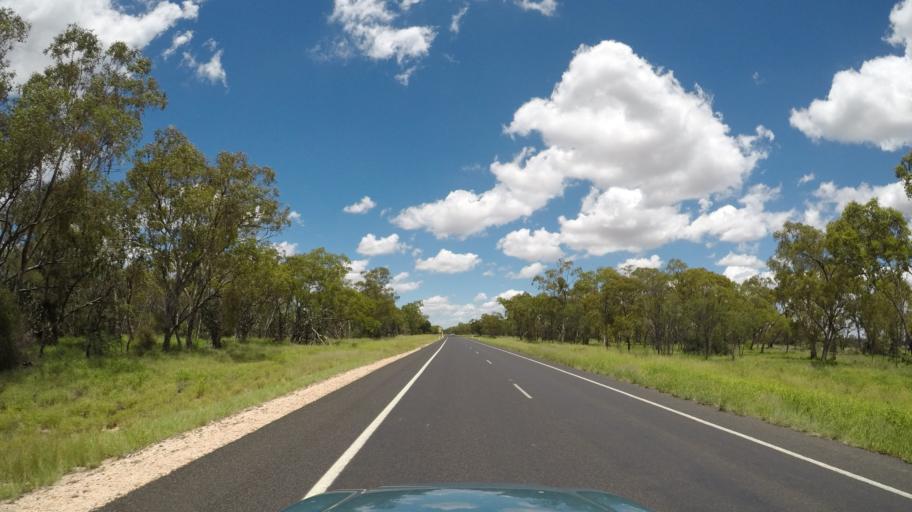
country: AU
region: Queensland
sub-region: Goondiwindi
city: Goondiwindi
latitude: -28.0752
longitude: 150.7458
